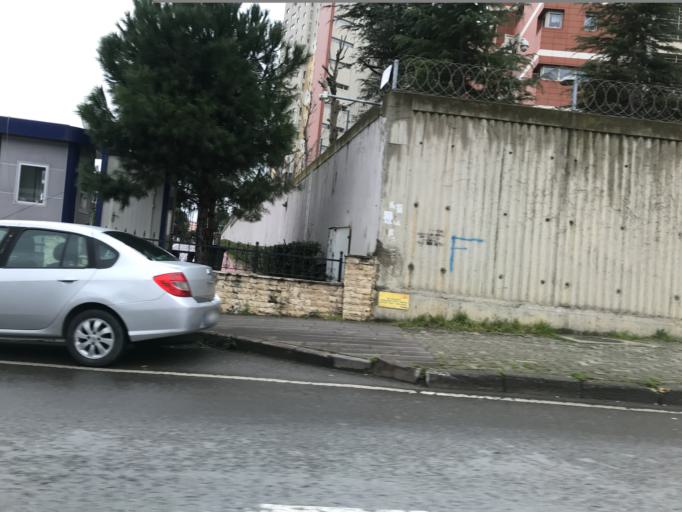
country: TR
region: Istanbul
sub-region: Atasehir
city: Atasehir
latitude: 40.9876
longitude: 29.1009
